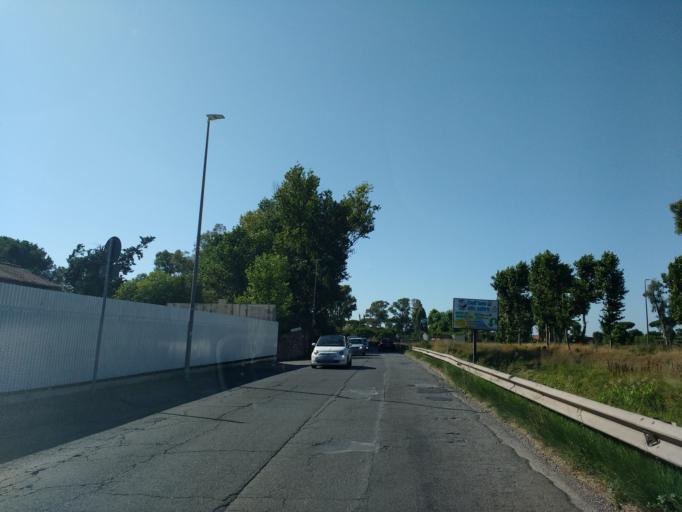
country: IT
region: Latium
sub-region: Citta metropolitana di Roma Capitale
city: Acilia-Castel Fusano-Ostia Antica
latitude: 41.7487
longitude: 12.3319
